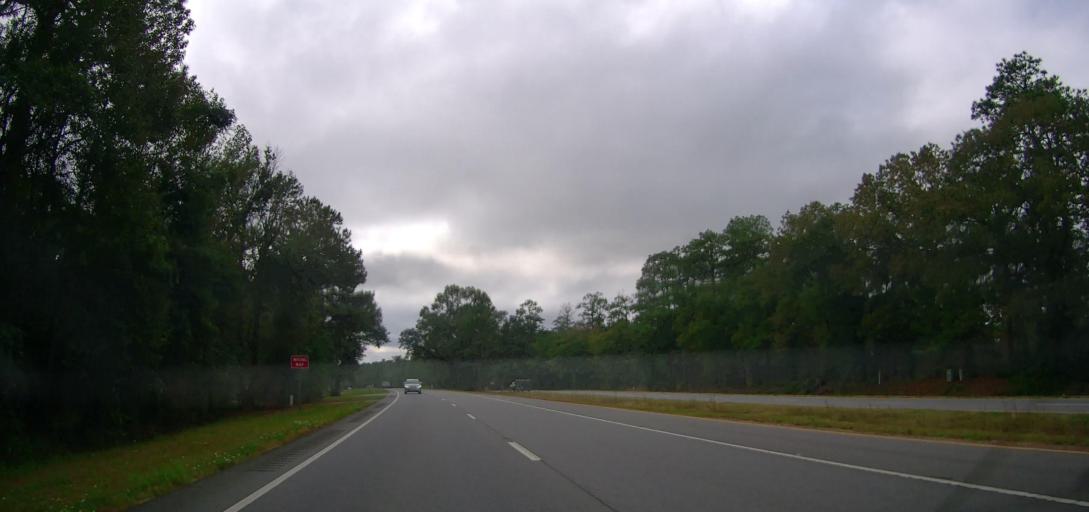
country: US
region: Georgia
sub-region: Grady County
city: Cairo
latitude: 30.7083
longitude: -84.1430
